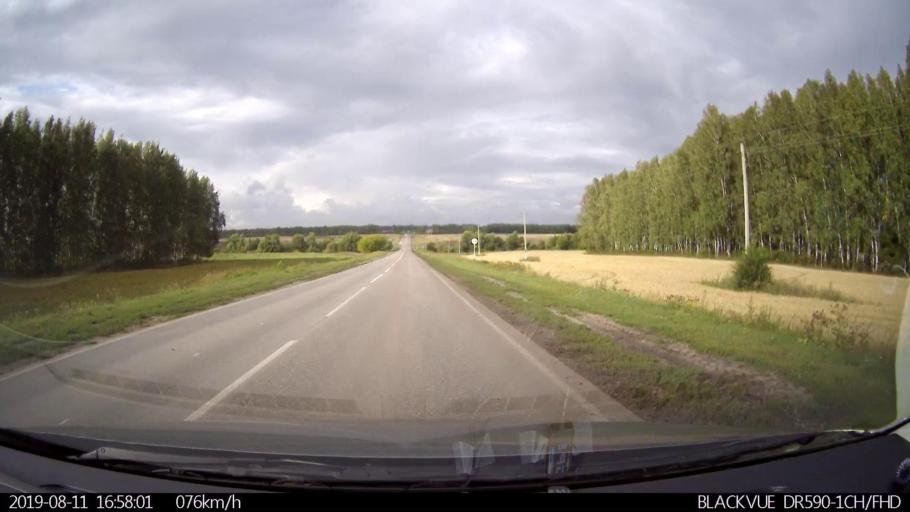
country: RU
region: Ulyanovsk
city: Mayna
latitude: 54.3041
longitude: 47.6550
